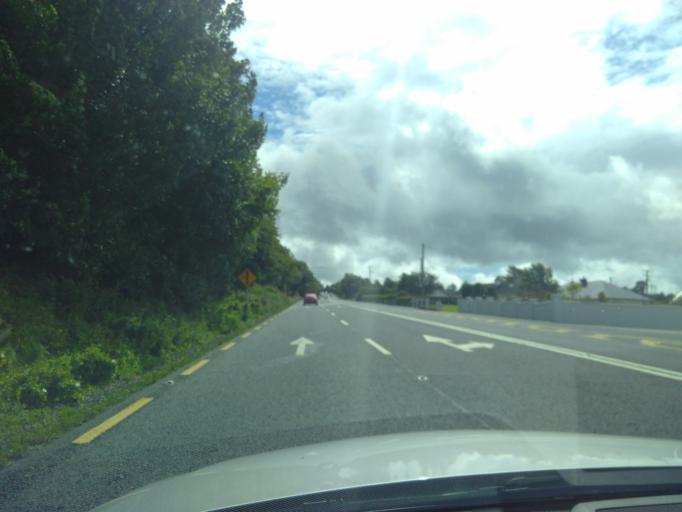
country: IE
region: Ulster
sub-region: County Donegal
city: Letterkenny
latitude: 54.9394
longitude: -7.6959
